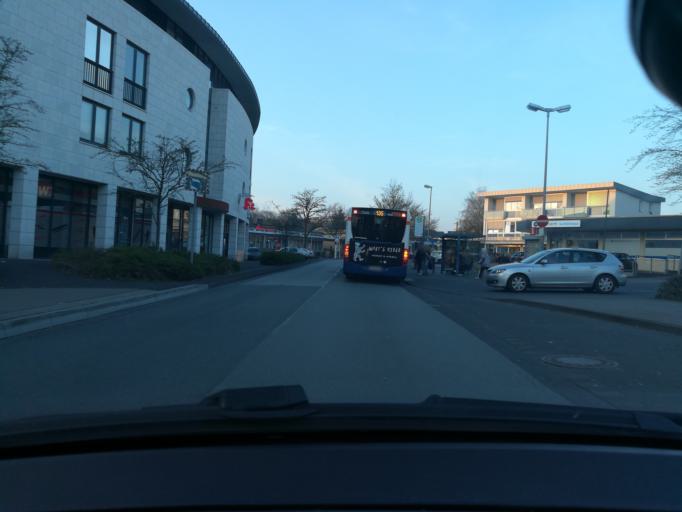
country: DE
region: North Rhine-Westphalia
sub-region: Regierungsbezirk Detmold
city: Oerlinghausen
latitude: 51.9456
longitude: 8.5859
